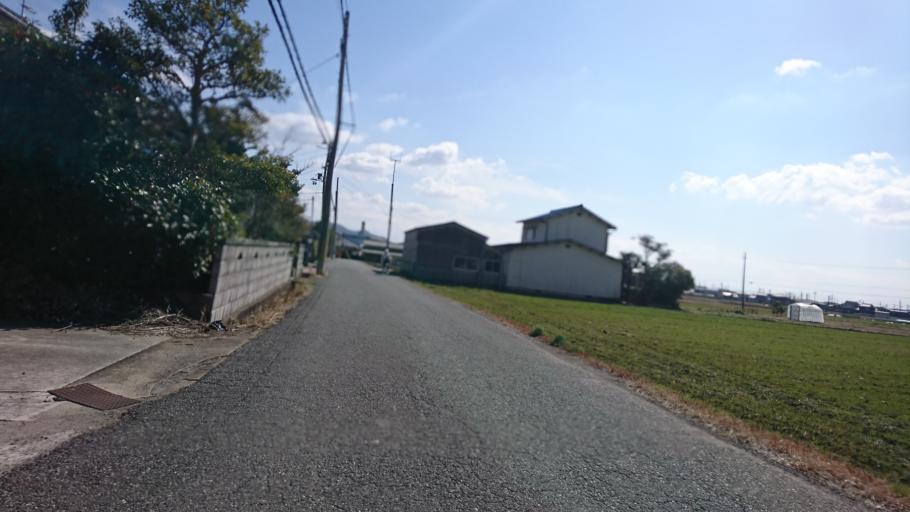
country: JP
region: Hyogo
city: Kakogawacho-honmachi
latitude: 34.8229
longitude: 134.8082
